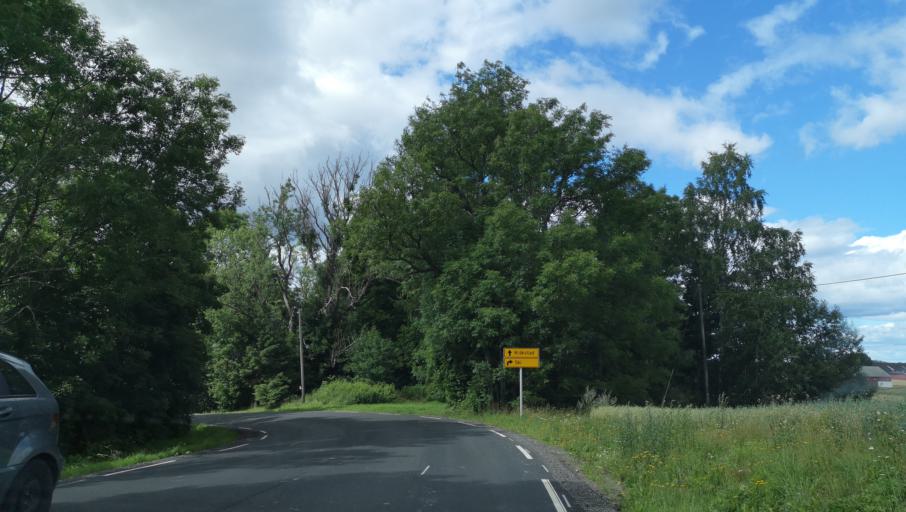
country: NO
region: Akershus
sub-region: Ski
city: Ski
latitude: 59.6939
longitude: 10.8997
